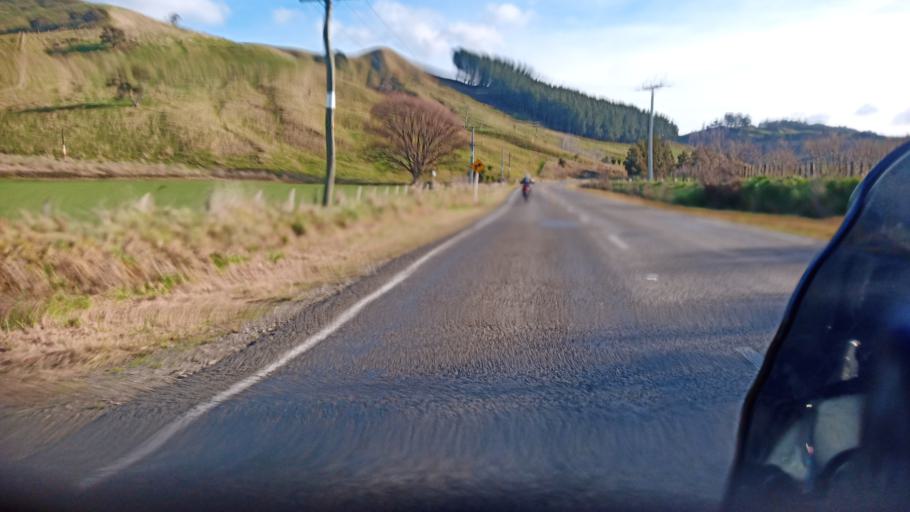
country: NZ
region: Gisborne
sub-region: Gisborne District
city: Gisborne
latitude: -38.4786
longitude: 177.8409
